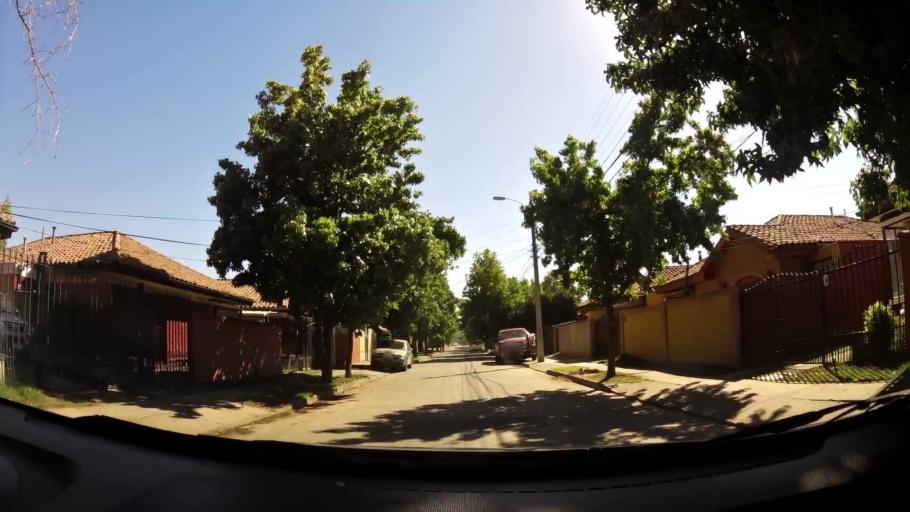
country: CL
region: O'Higgins
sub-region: Provincia de Cachapoal
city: Rancagua
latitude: -34.1787
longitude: -70.7059
